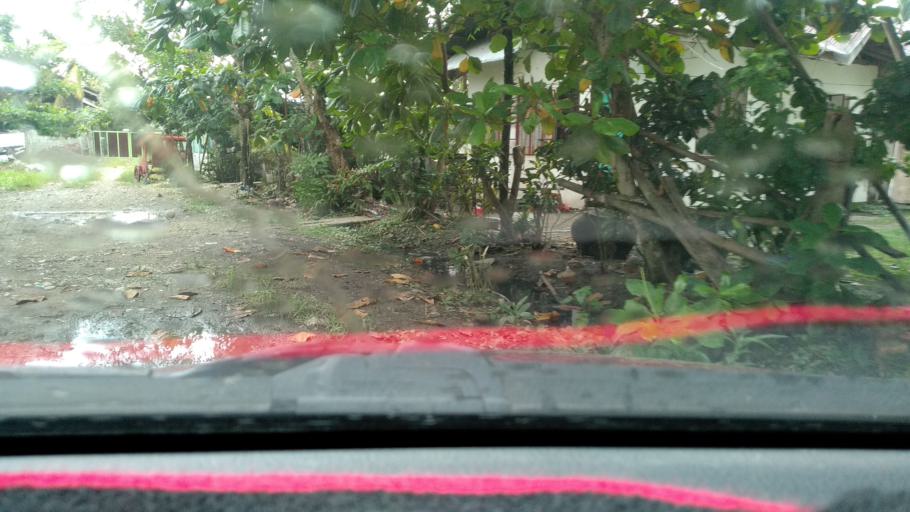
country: PH
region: Caraga
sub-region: Province of Agusan del Sur
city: Patin-ay
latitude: 8.5489
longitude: 125.9371
